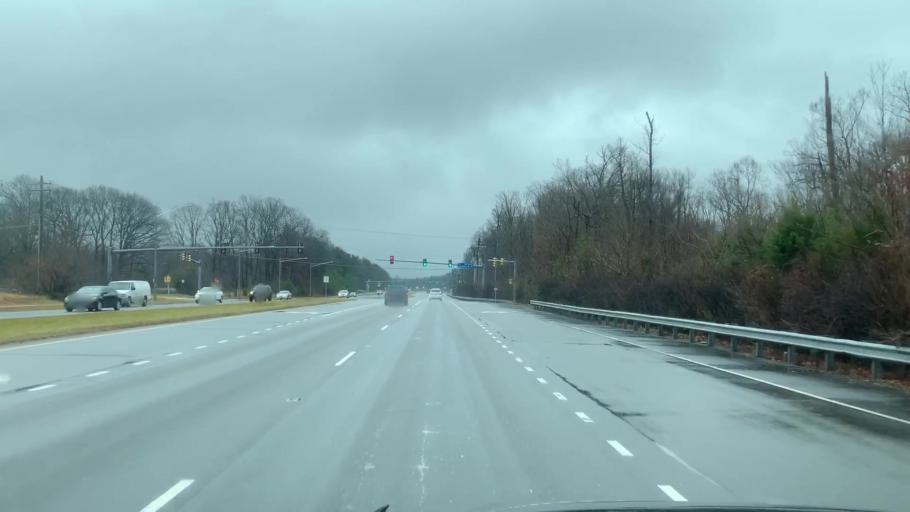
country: US
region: Virginia
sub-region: Fairfax County
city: Fairfax Station
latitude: 38.7633
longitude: -77.3110
